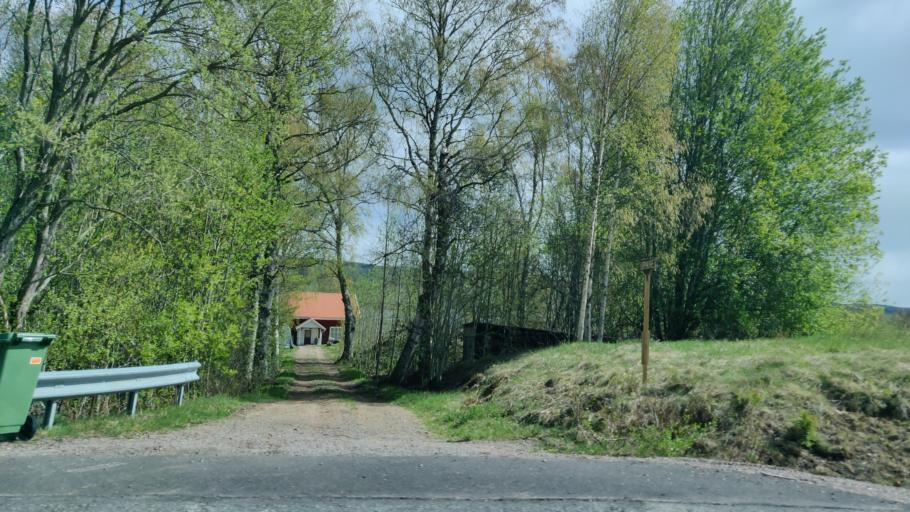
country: SE
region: Vaermland
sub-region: Munkfors Kommun
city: Munkfors
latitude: 59.8587
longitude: 13.7065
